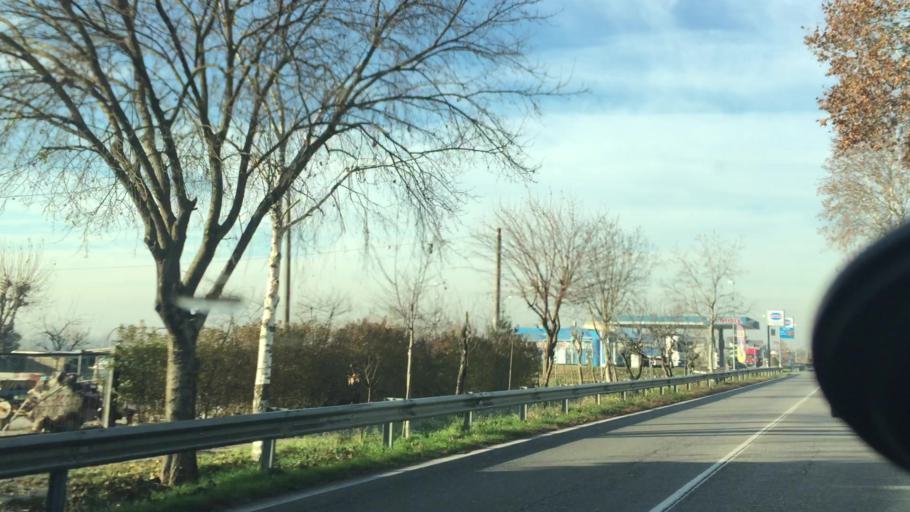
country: IT
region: Lombardy
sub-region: Provincia di Bergamo
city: Badalasco
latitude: 45.5239
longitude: 9.5553
